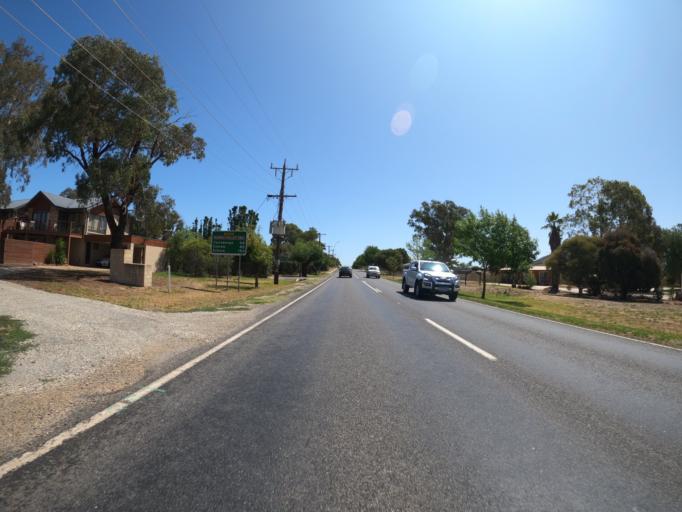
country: AU
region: New South Wales
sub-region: Corowa Shire
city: Corowa
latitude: -36.0526
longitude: 146.4516
